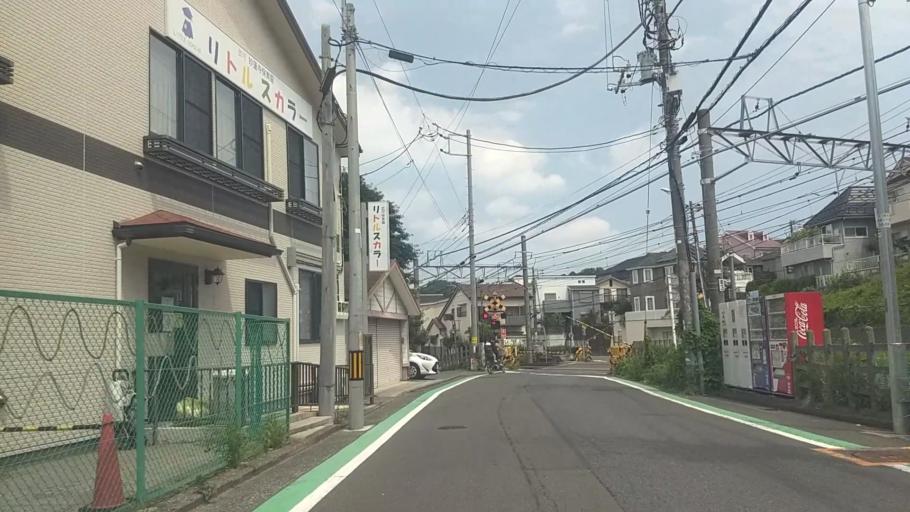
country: JP
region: Kanagawa
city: Yokohama
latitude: 35.5030
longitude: 139.6344
